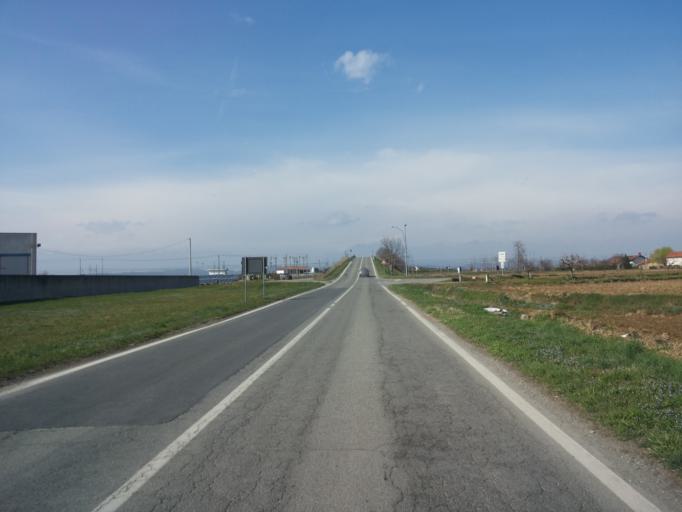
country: IT
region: Piedmont
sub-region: Provincia di Vercelli
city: Bianze
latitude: 45.3039
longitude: 8.1119
